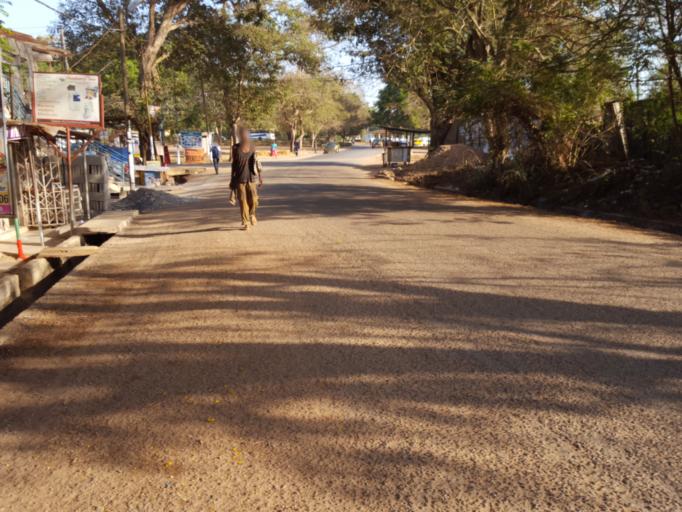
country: GH
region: Central
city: Cape Coast
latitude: 5.1146
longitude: -1.2919
